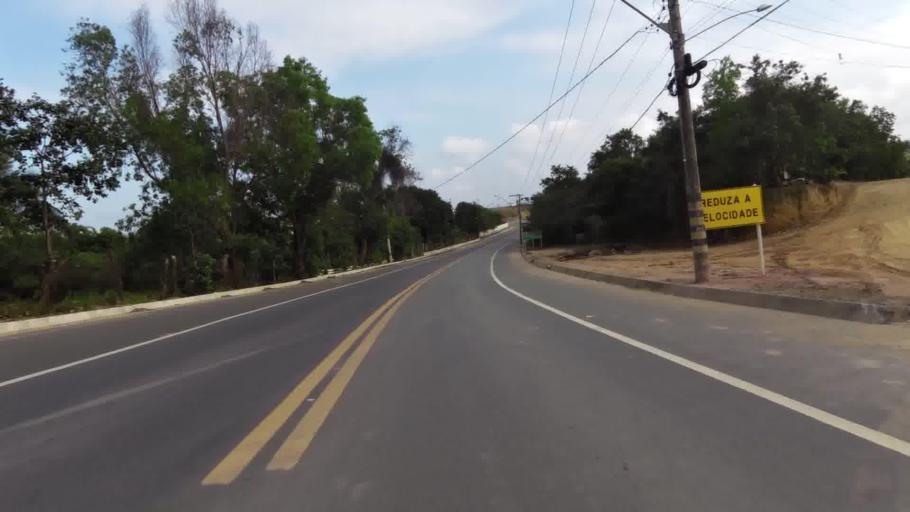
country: BR
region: Espirito Santo
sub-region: Piuma
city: Piuma
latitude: -20.8222
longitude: -40.6253
